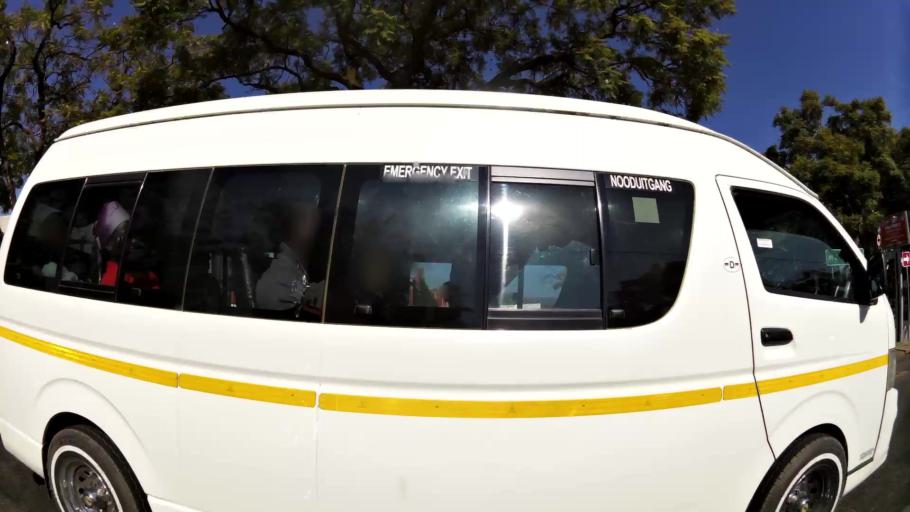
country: ZA
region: Gauteng
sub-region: City of Tshwane Metropolitan Municipality
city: Pretoria
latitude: -25.7456
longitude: 28.2225
